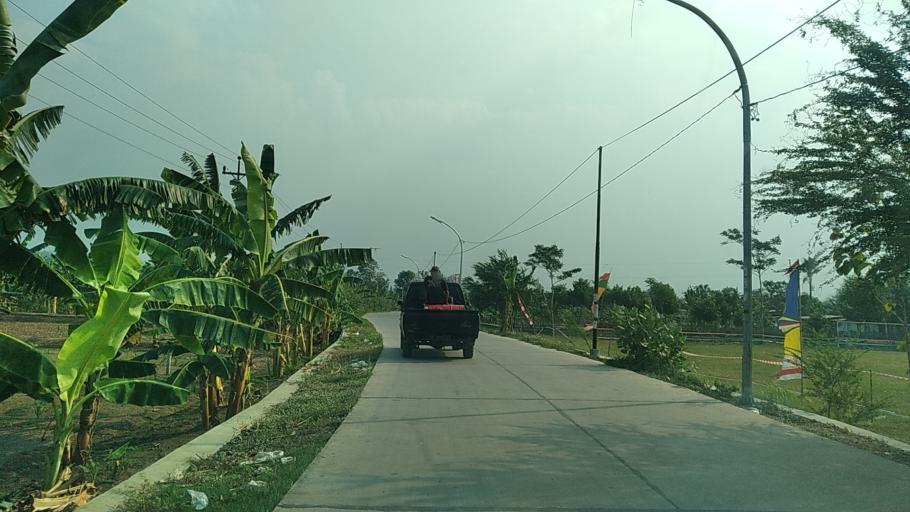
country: ID
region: Central Java
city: Mranggen
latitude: -7.0709
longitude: 110.4681
